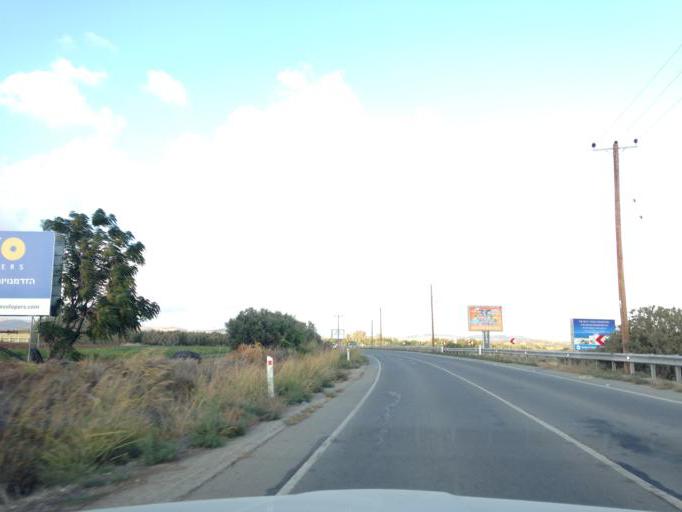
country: CY
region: Pafos
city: Paphos
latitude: 34.7101
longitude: 32.5092
